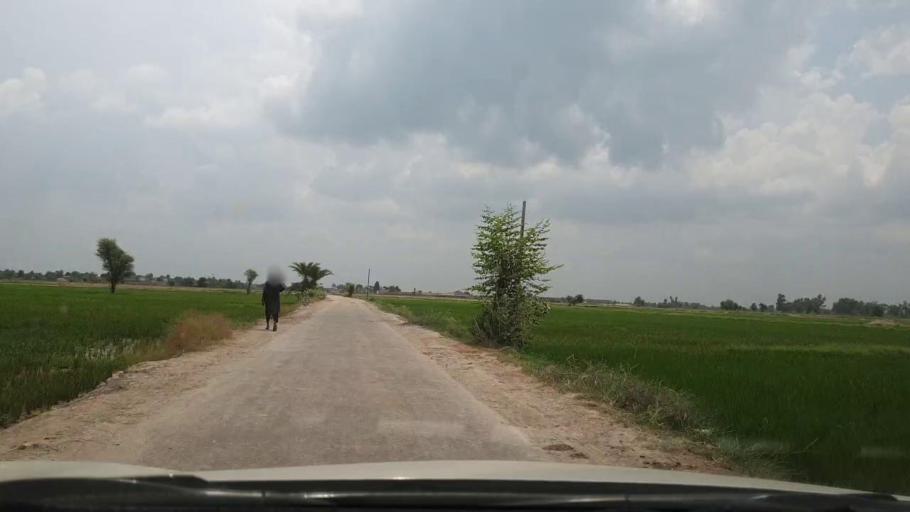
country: PK
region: Sindh
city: Goth Garelo
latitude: 27.4266
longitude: 68.1073
